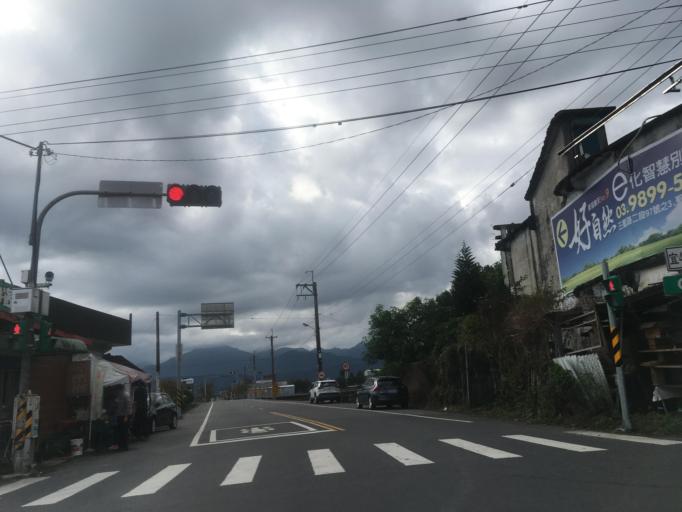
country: TW
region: Taiwan
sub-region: Yilan
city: Yilan
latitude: 24.6860
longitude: 121.7133
